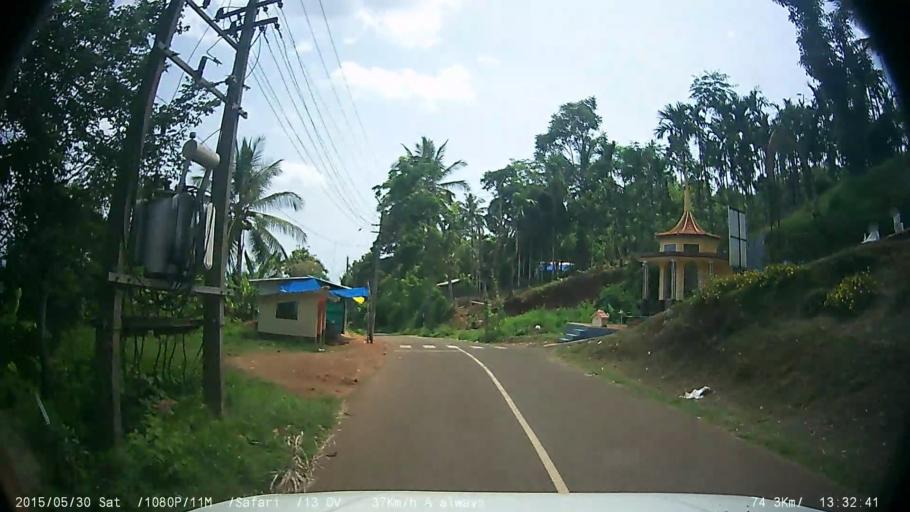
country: IN
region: Kerala
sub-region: Wayanad
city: Panamaram
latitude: 11.8202
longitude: 76.0776
